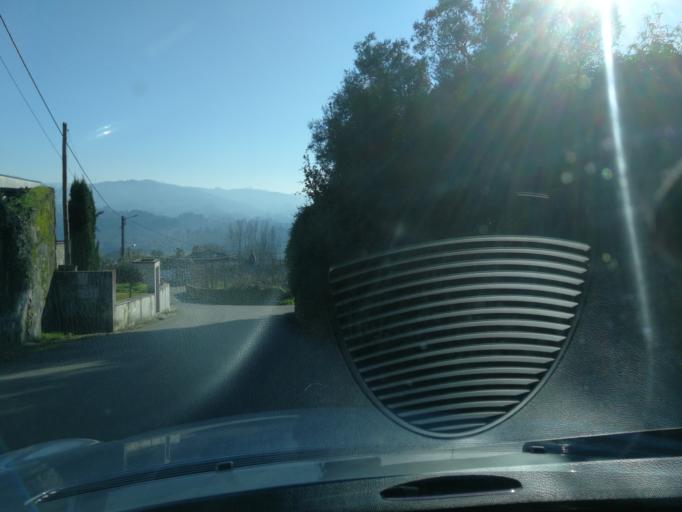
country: PT
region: Braga
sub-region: Braga
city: Adaufe
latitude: 41.6137
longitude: -8.3979
